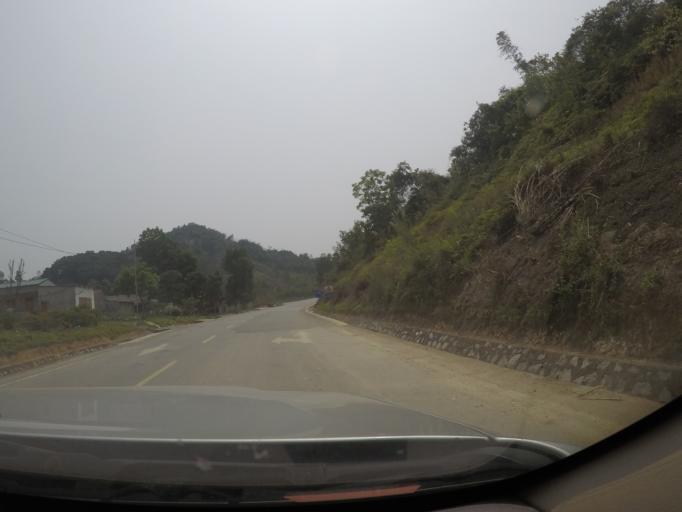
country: VN
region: Thanh Hoa
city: Thi Tran Yen Cat
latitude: 19.6780
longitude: 105.4555
